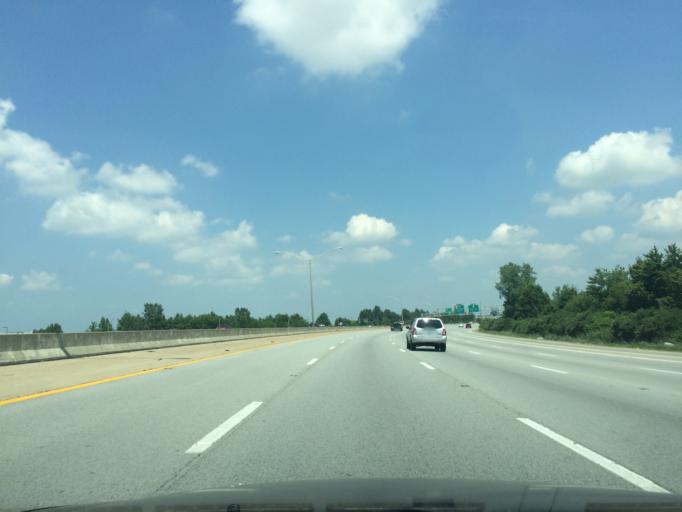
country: US
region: Kentucky
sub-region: Jefferson County
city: Heritage Creek
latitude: 38.1601
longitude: -85.7198
